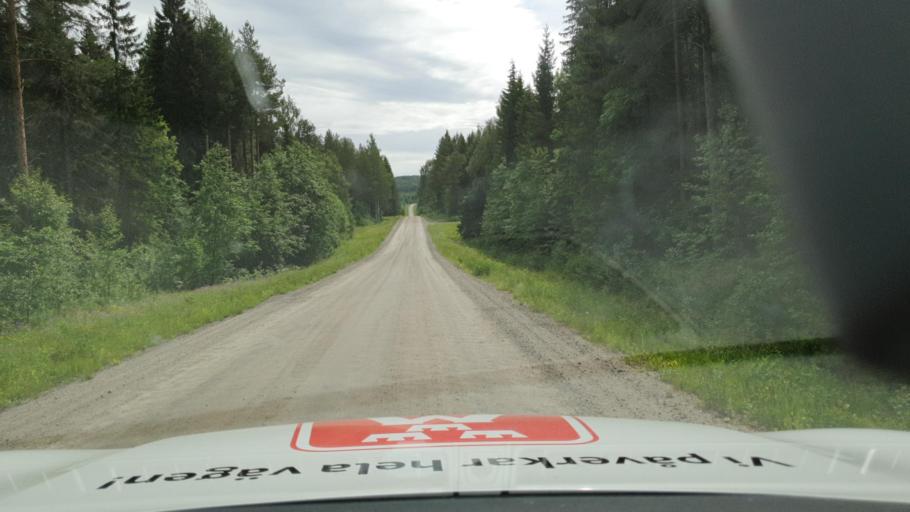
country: SE
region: Vaesterbotten
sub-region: Skelleftea Kommun
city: Burtraesk
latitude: 64.3839
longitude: 20.4195
